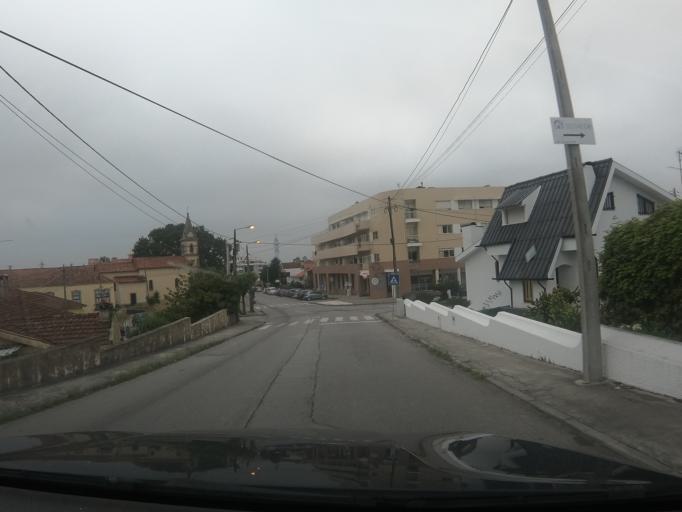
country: PT
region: Aveiro
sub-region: Santa Maria da Feira
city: Pacos de Brandao
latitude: 40.9847
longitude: -8.5969
